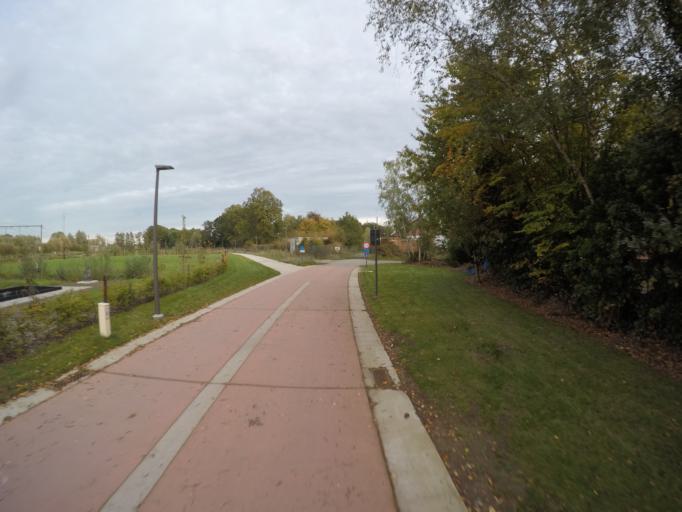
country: BE
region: Flanders
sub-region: Provincie Antwerpen
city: Zwijndrecht
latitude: 51.2116
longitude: 4.3029
